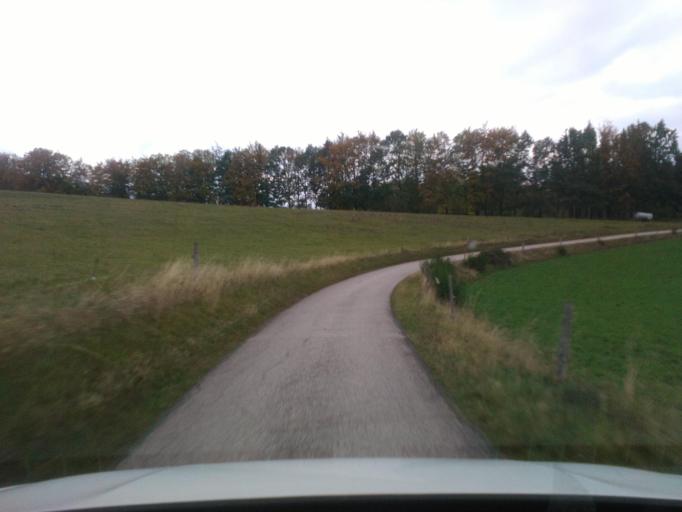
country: FR
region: Lorraine
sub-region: Departement des Vosges
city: Senones
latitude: 48.3734
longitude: 7.0277
